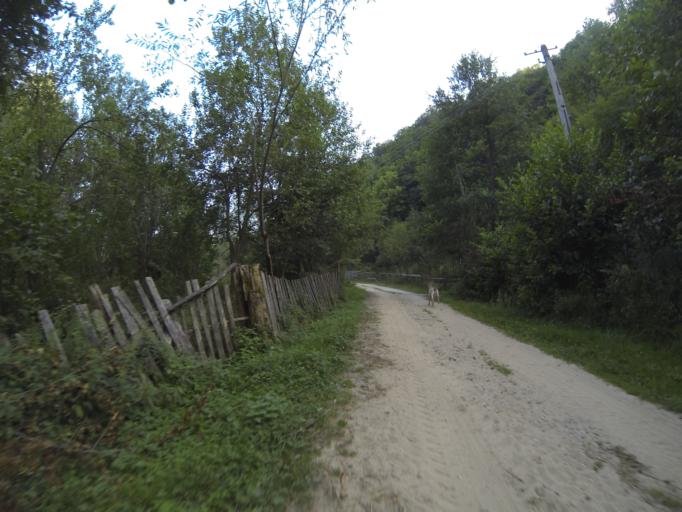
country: RO
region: Valcea
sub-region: Comuna Horezu
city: Horezu
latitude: 45.1890
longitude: 23.9861
